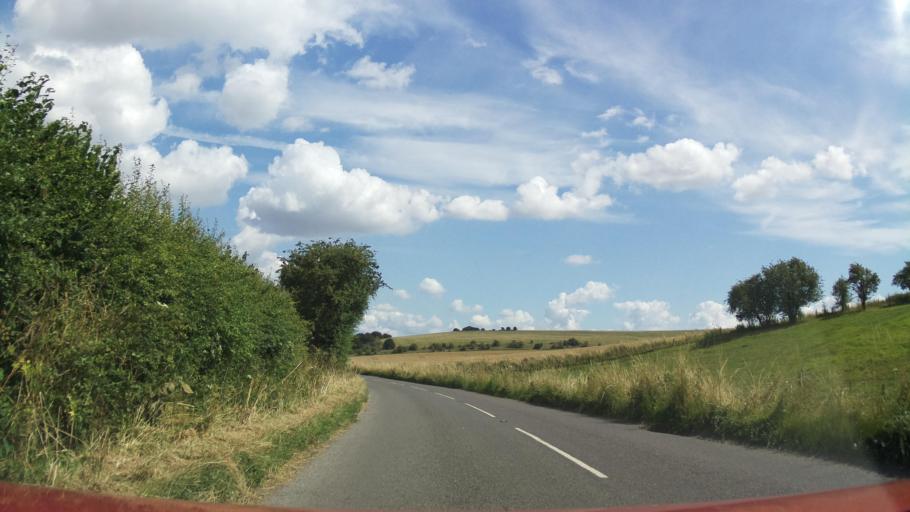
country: GB
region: England
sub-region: West Berkshire
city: Lambourn
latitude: 51.5198
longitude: -1.5715
